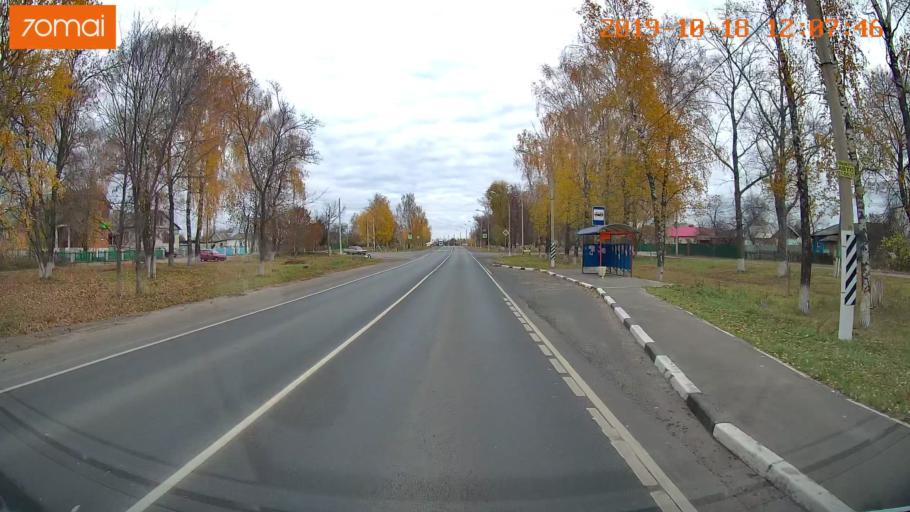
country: RU
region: Rjazan
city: Zakharovo
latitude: 54.3712
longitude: 39.2846
